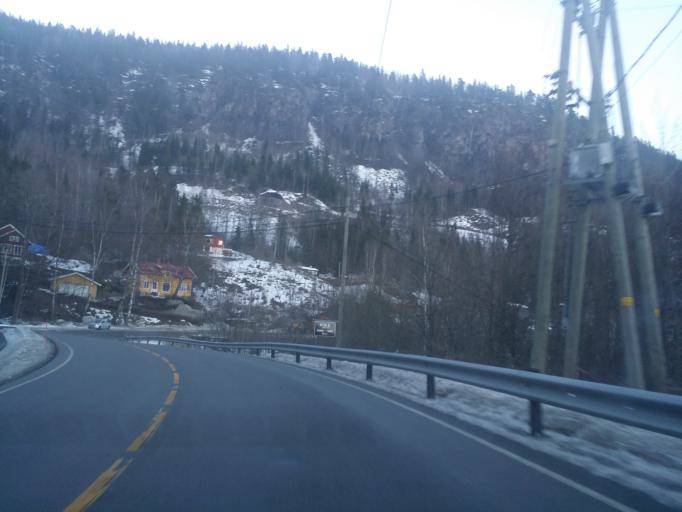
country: NO
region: Buskerud
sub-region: Hole
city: Vik
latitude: 60.0002
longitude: 10.2804
